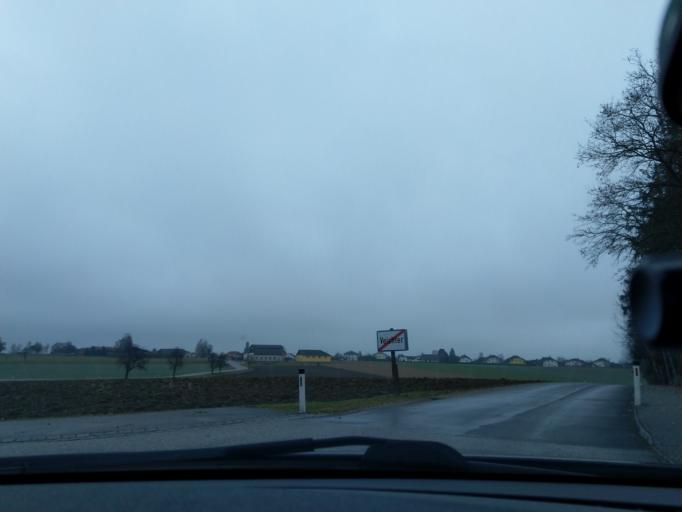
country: AT
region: Upper Austria
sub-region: Politischer Bezirk Urfahr-Umgebung
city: Engerwitzdorf
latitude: 48.3727
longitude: 14.5221
